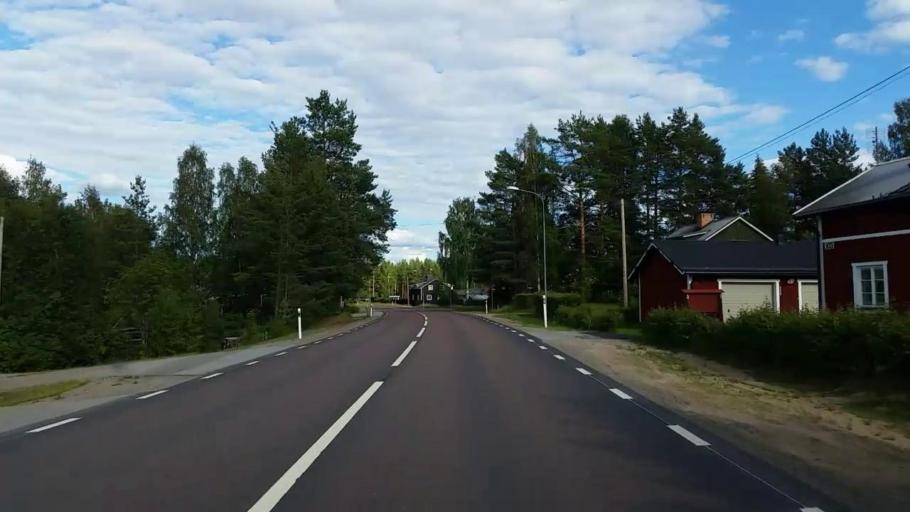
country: SE
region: Gaevleborg
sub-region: Ljusdals Kommun
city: Ljusdal
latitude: 61.8354
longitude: 16.0140
